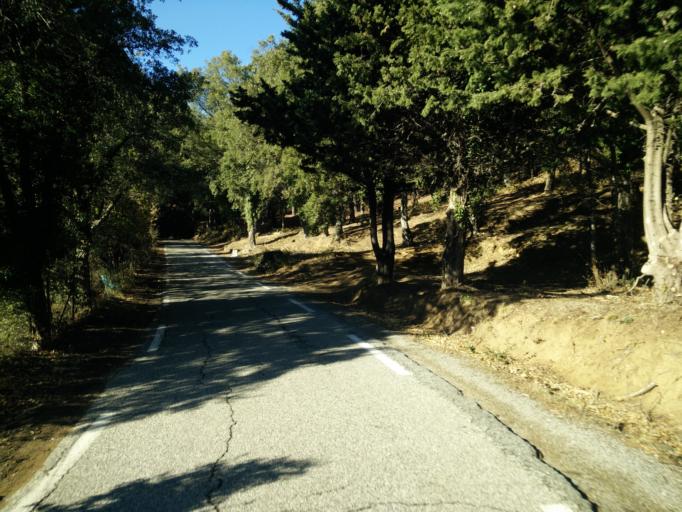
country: FR
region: Provence-Alpes-Cote d'Azur
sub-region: Departement du Var
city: La Garde-Freinet
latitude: 43.2571
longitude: 6.4119
